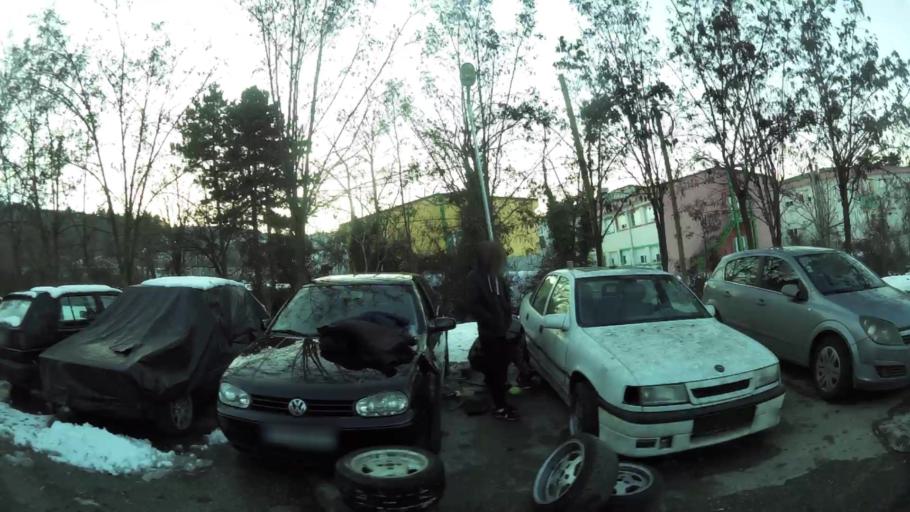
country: MK
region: Karpos
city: Skopje
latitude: 41.9898
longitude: 21.4059
